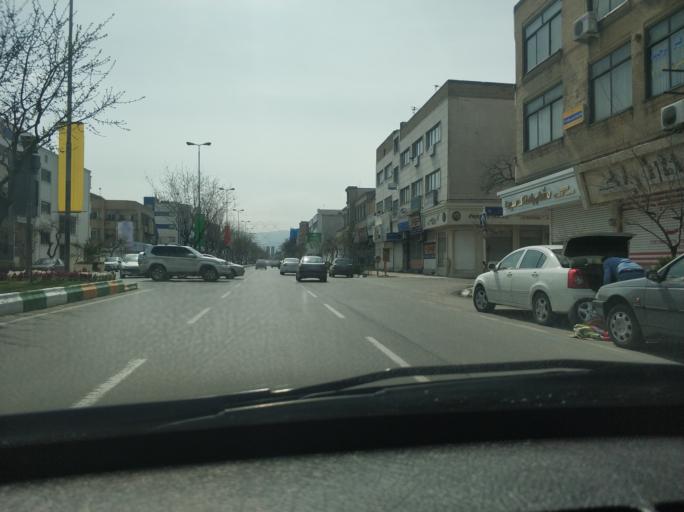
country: IR
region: Razavi Khorasan
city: Mashhad
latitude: 36.3039
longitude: 59.5651
